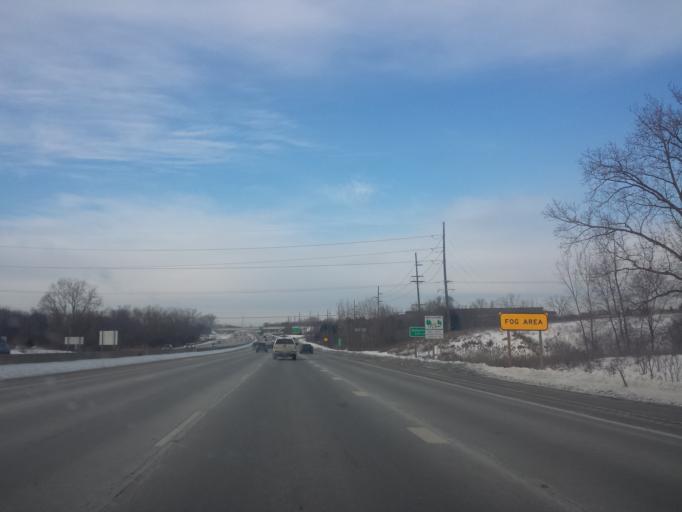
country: US
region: Michigan
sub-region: Oakland County
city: Auburn Hills
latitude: 42.6446
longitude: -83.2087
